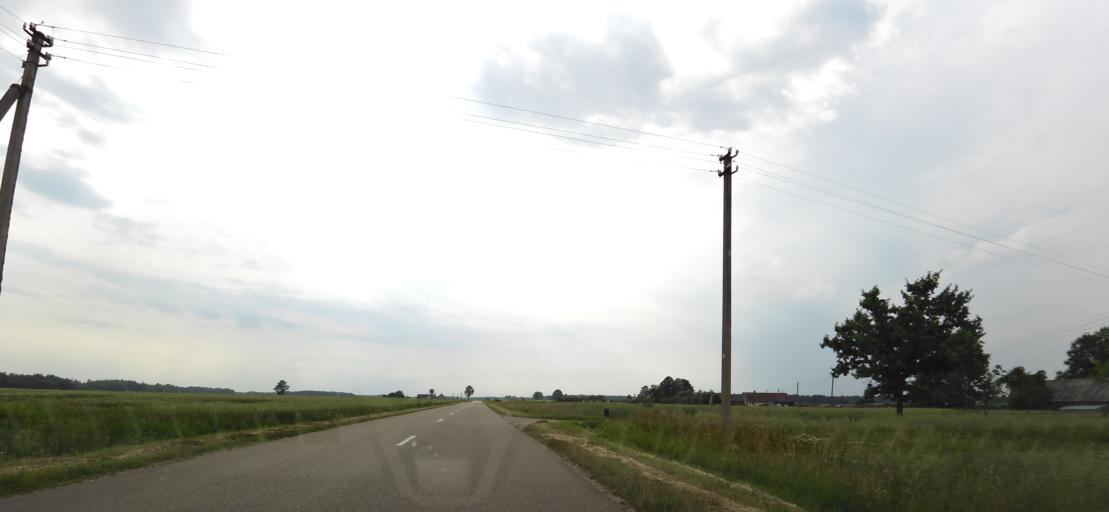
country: LT
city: Obeliai
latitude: 56.1187
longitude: 25.1082
